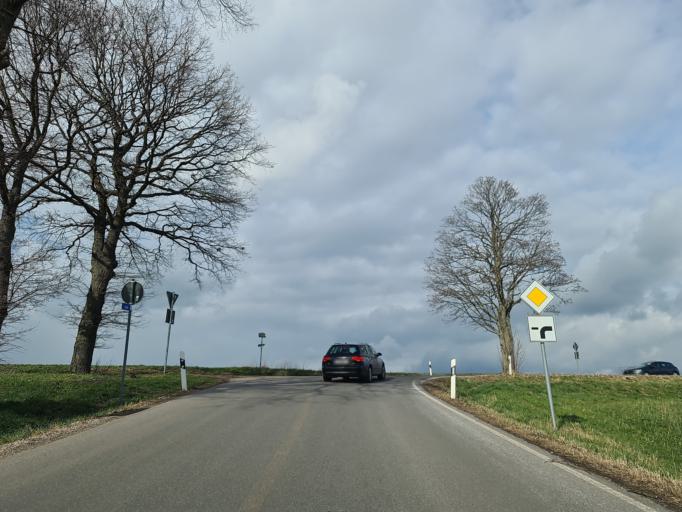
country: DE
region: Saxony
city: Lichtenstein
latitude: 50.7180
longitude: 12.6232
